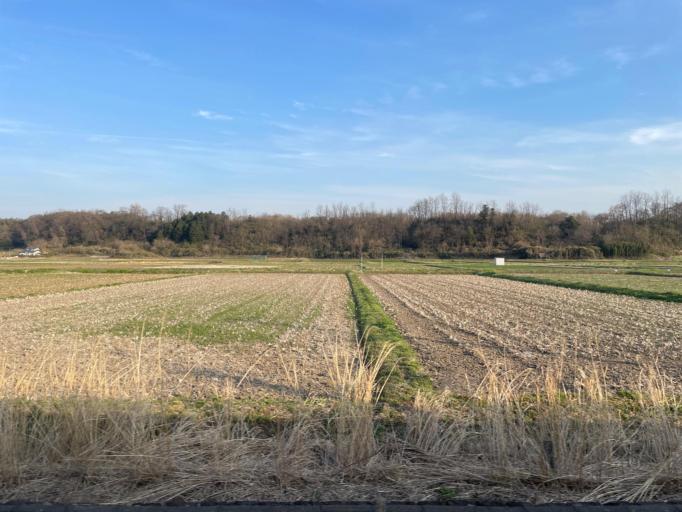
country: JP
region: Gunma
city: Annaka
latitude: 36.3094
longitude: 138.8783
